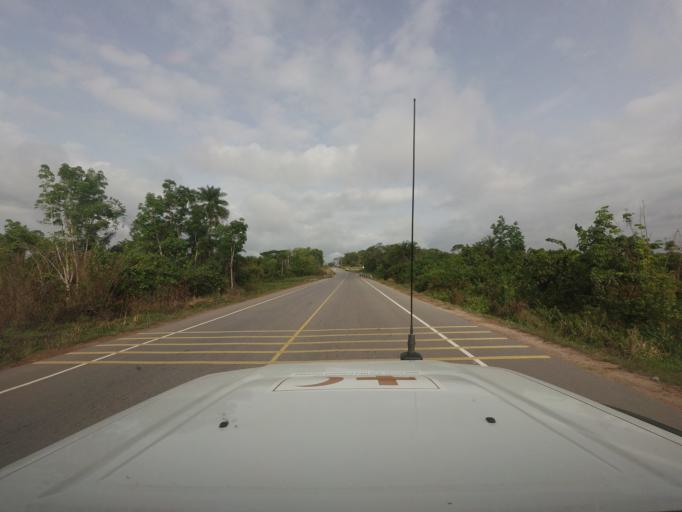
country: LR
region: Bong
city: Gbarnga
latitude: 7.0029
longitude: -9.2944
